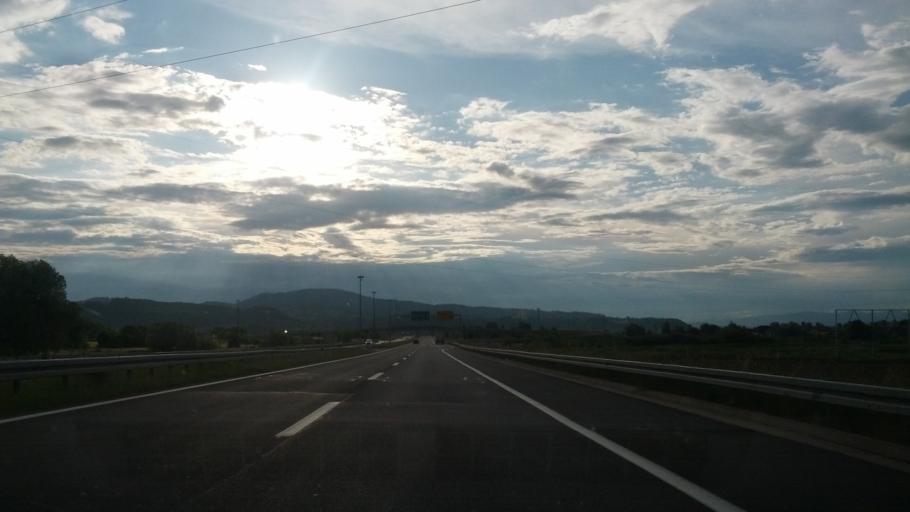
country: HR
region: Zagrebacka
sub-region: Grad Samobor
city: Samobor
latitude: 45.8300
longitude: 15.7283
